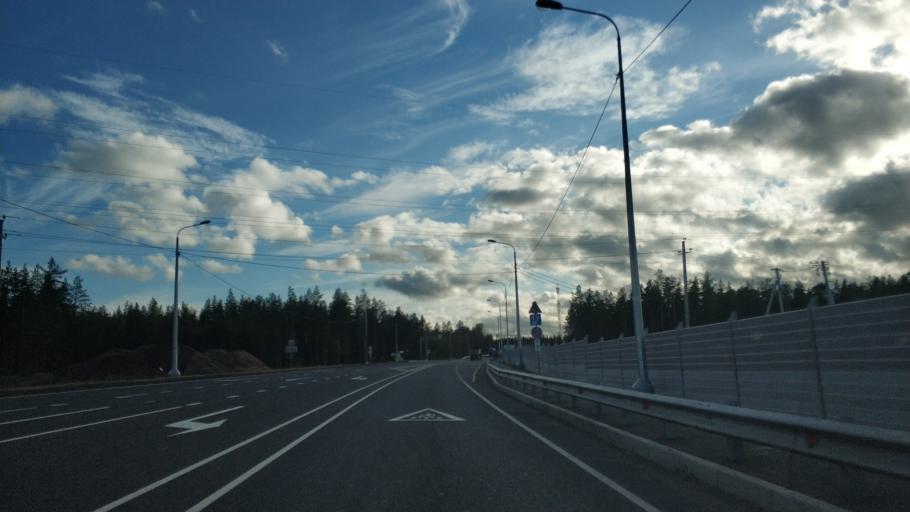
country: RU
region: Leningrad
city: Priozersk
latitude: 60.8474
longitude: 30.1446
